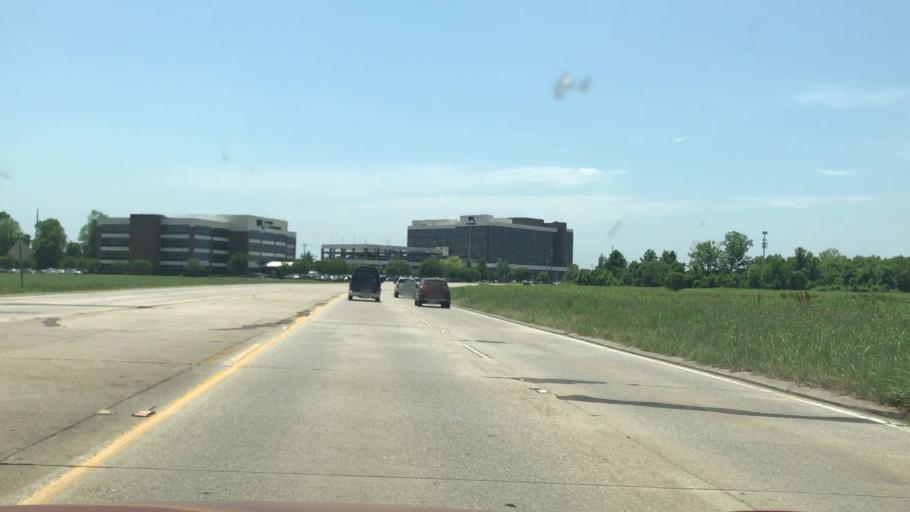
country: US
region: Louisiana
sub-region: Bossier Parish
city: Bossier City
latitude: 32.4367
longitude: -93.7072
